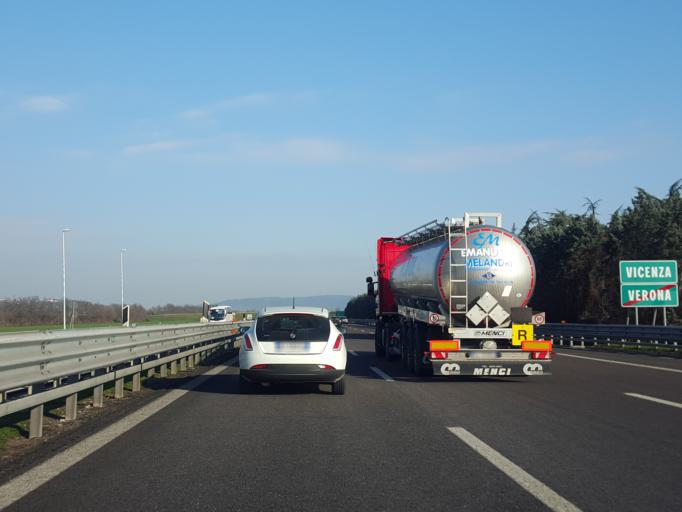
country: IT
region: Veneto
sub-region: Provincia di Verona
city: Locara
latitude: 45.4276
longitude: 11.3359
